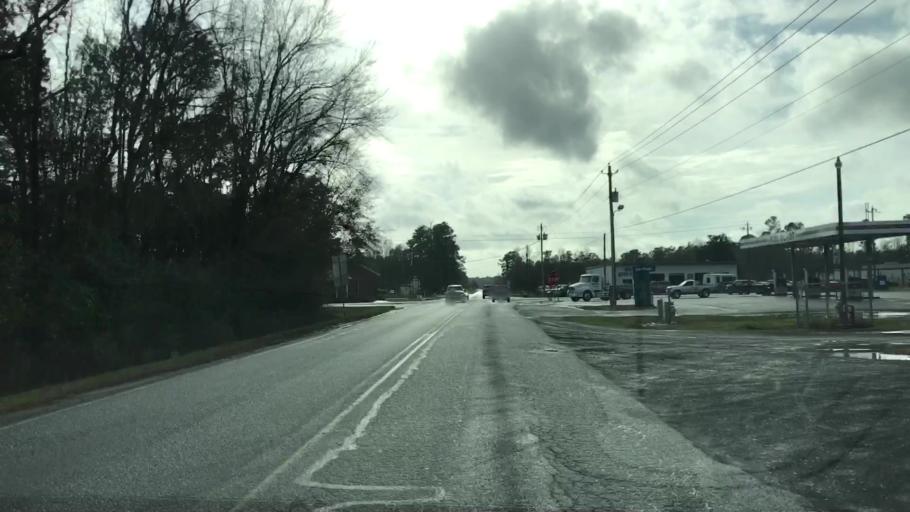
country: US
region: South Carolina
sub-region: Williamsburg County
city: Andrews
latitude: 33.4536
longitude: -79.5799
